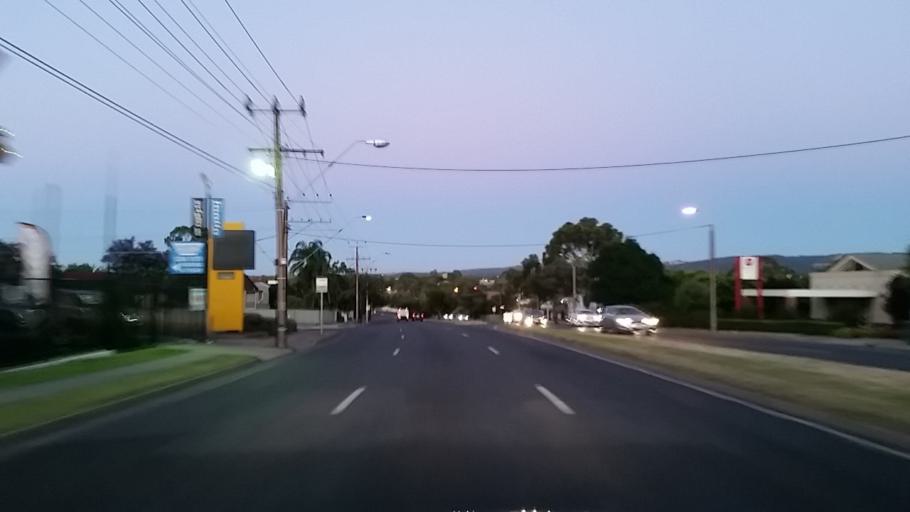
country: AU
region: South Australia
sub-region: Port Adelaide Enfield
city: Gilles Plains
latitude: -34.8522
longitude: 138.6660
